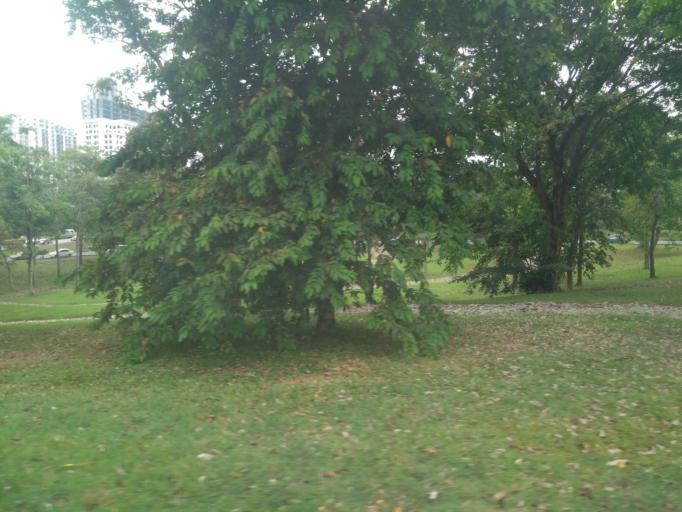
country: MY
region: Johor
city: Johor Bahru
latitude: 1.4883
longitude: 103.7403
